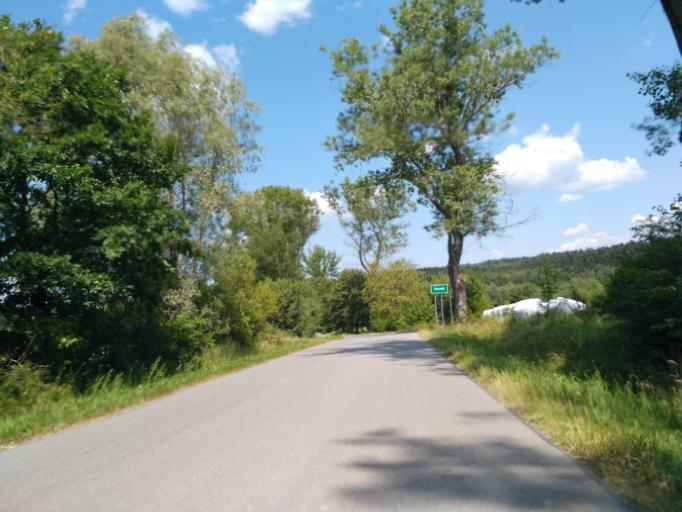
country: PL
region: Subcarpathian Voivodeship
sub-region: Powiat sanocki
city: Poraz
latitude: 49.4798
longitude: 22.1904
